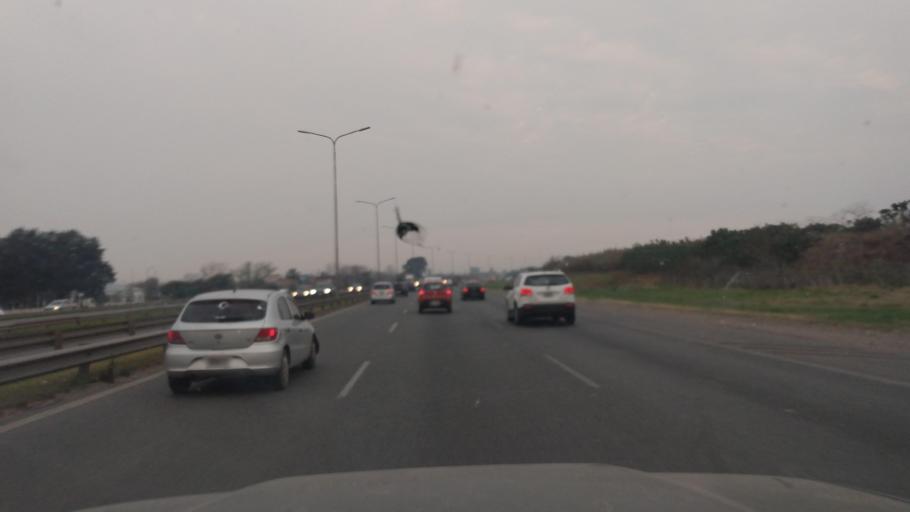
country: AR
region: Buenos Aires
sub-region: Partido de Tigre
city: Tigre
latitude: -34.4969
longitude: -58.5930
